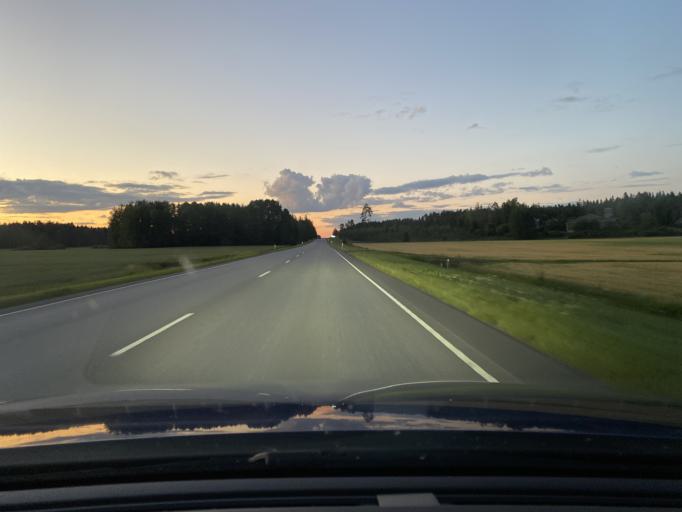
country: FI
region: Varsinais-Suomi
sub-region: Loimaa
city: Poeytyae
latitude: 60.8040
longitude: 22.6339
